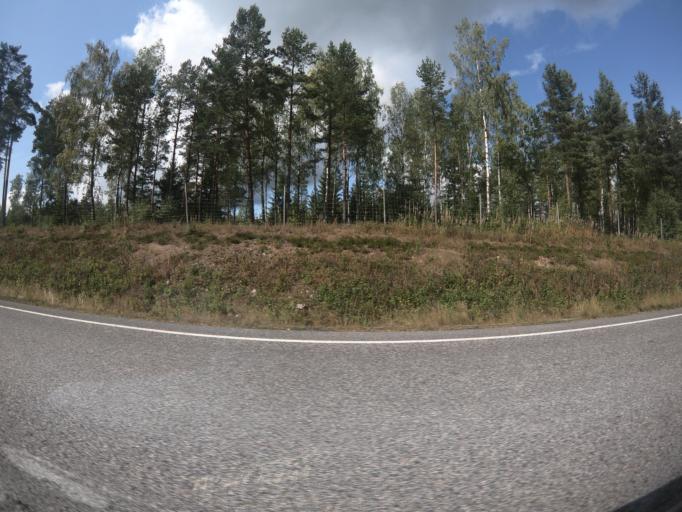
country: SE
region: Kronoberg
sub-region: Vaxjo Kommun
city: Braas
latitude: 57.0159
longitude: 15.0530
